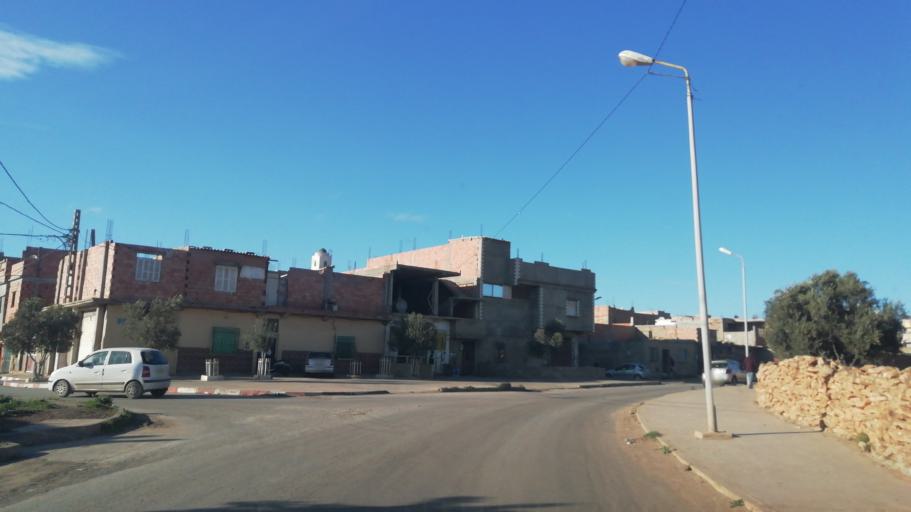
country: DZ
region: Oran
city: Sidi ech Chahmi
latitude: 35.6886
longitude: -0.4963
